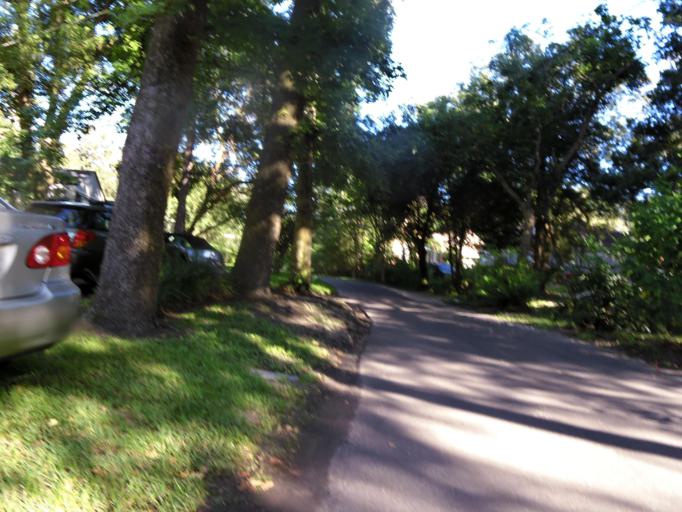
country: US
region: Florida
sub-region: Duval County
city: Jacksonville
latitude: 30.2996
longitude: -81.7154
